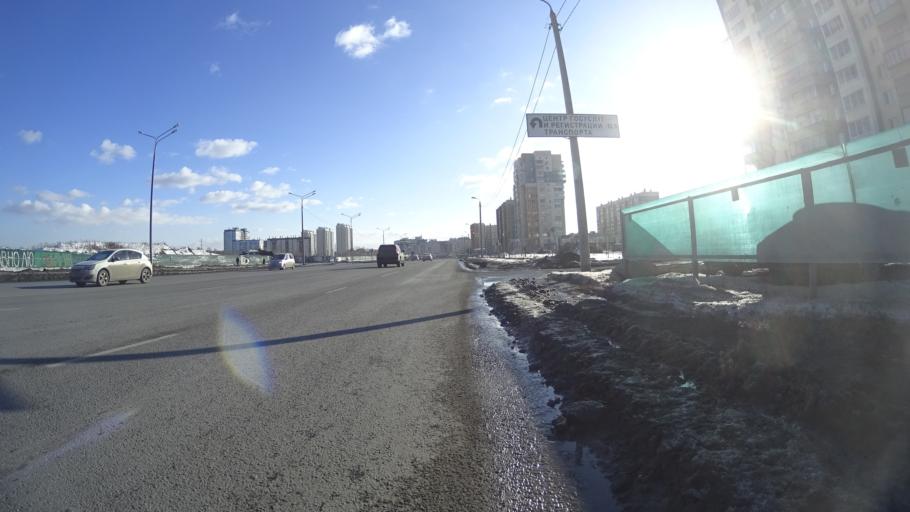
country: RU
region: Chelyabinsk
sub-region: Gorod Chelyabinsk
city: Chelyabinsk
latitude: 55.1646
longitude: 61.3024
